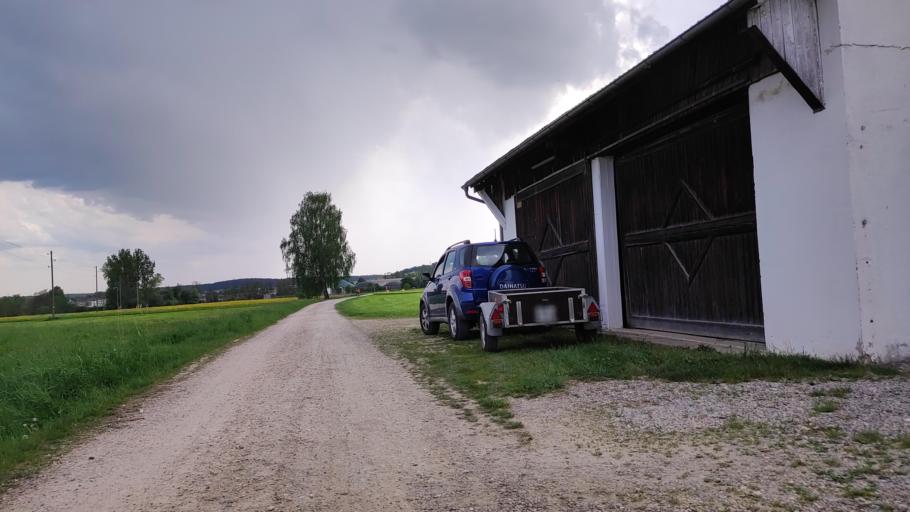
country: DE
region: Bavaria
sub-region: Swabia
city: Altenmunster
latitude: 48.4771
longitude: 10.5950
